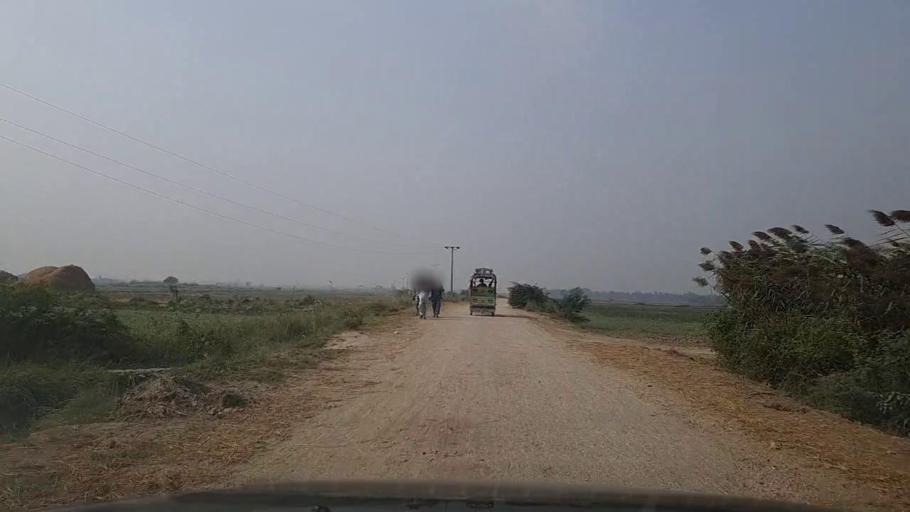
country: PK
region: Sindh
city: Mirpur Sakro
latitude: 24.5473
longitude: 67.8317
